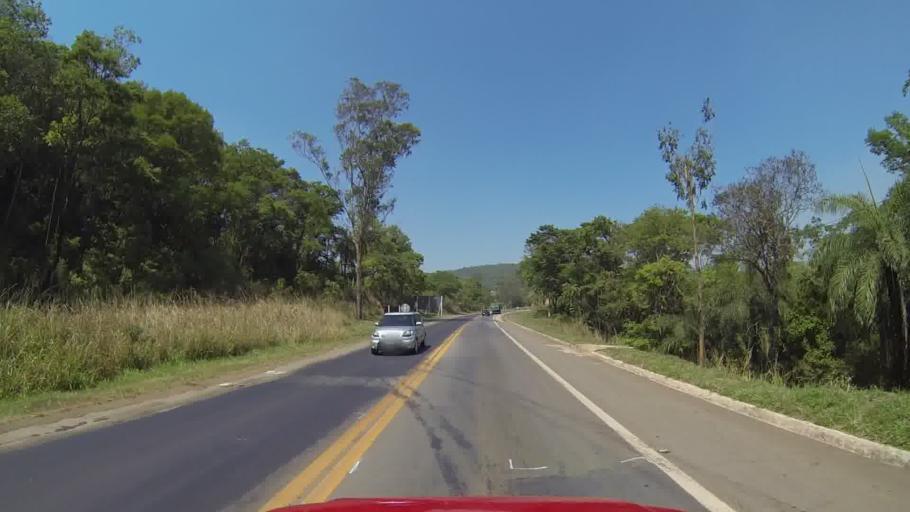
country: BR
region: Minas Gerais
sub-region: Mateus Leme
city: Mateus Leme
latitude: -20.0236
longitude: -44.5019
